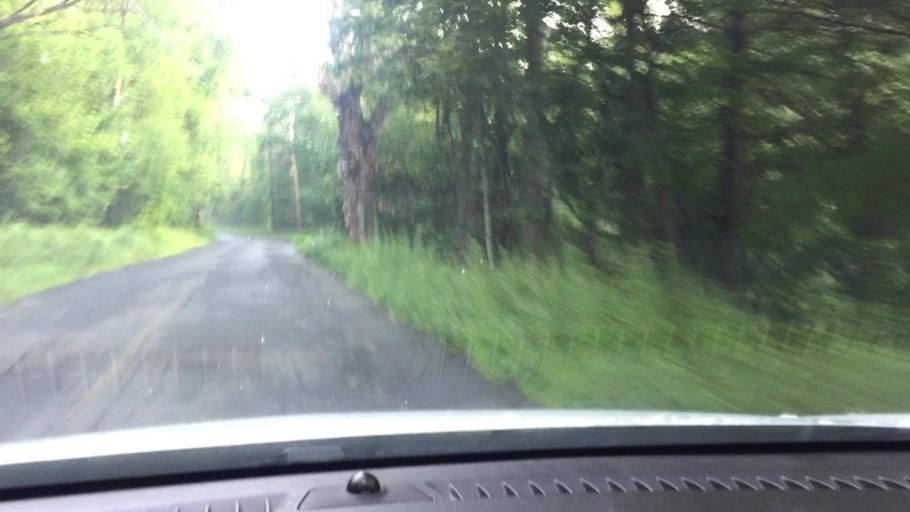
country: US
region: Massachusetts
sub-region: Hampshire County
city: Chesterfield
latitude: 42.3162
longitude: -72.9245
